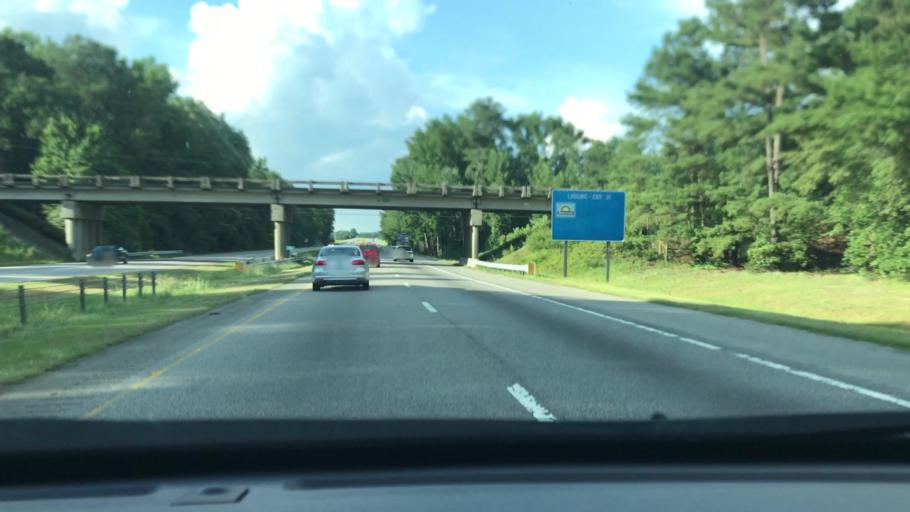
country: US
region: North Carolina
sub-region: Robeson County
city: Saint Pauls
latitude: 34.7991
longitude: -78.9913
